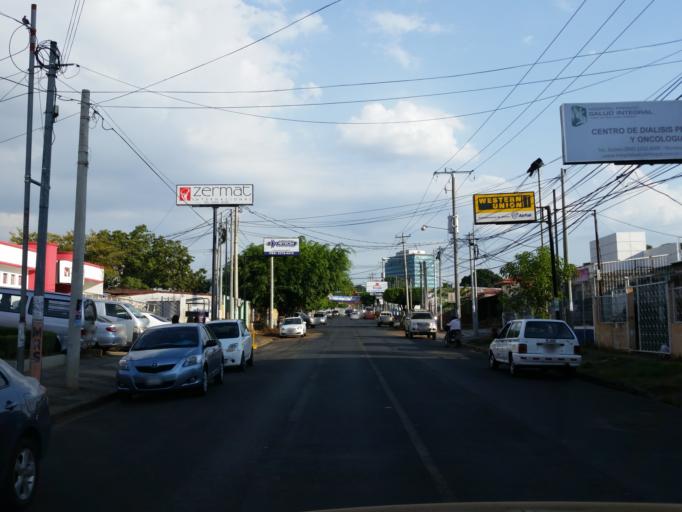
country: NI
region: Managua
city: Managua
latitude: 12.1290
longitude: -86.2621
